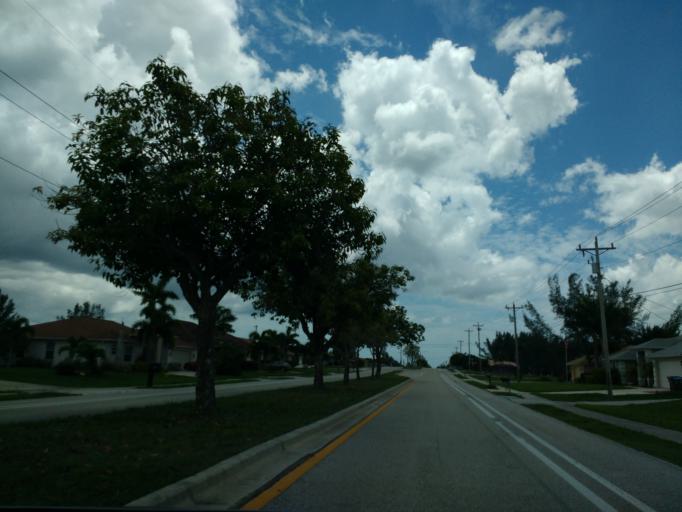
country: US
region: Florida
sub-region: Lee County
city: Cape Coral
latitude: 26.5695
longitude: -82.0174
